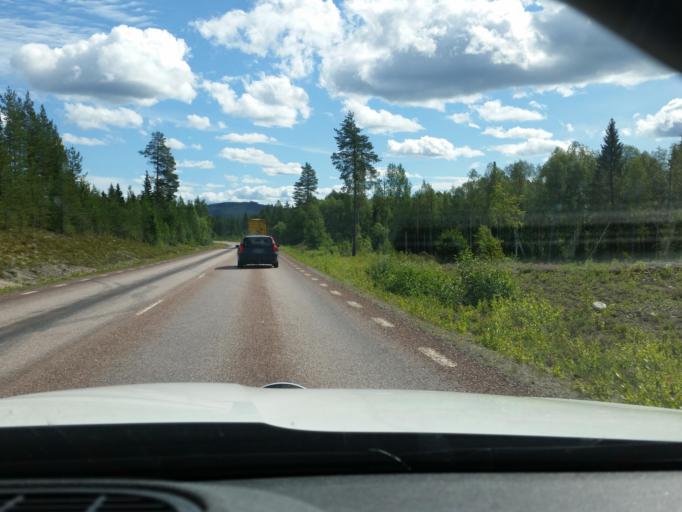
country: SE
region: Norrbotten
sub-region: Alvsbyns Kommun
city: AElvsbyn
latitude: 65.6725
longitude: 21.1443
